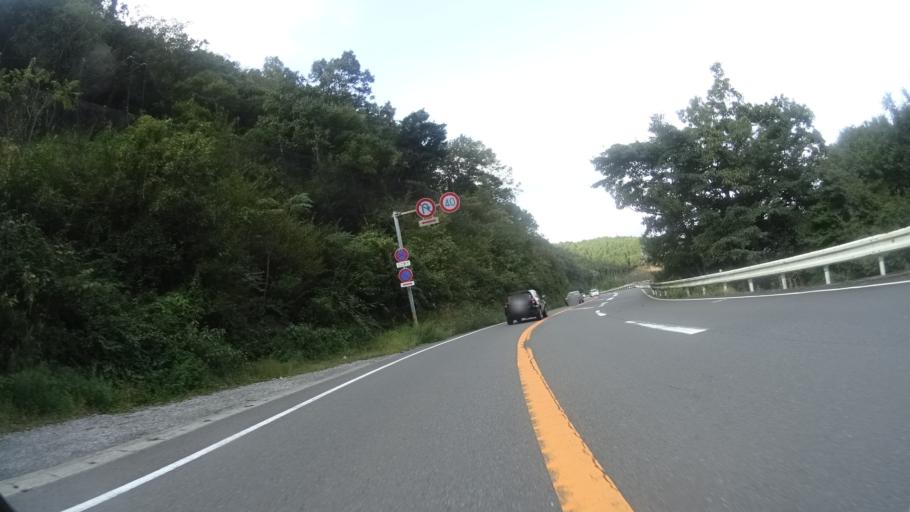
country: JP
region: Oita
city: Beppu
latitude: 33.2816
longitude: 131.4512
